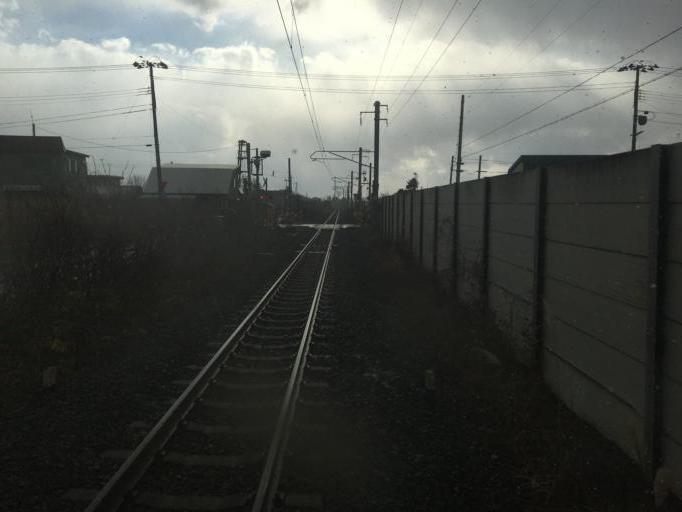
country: JP
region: Aomori
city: Aomori Shi
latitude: 40.9666
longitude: 140.6547
